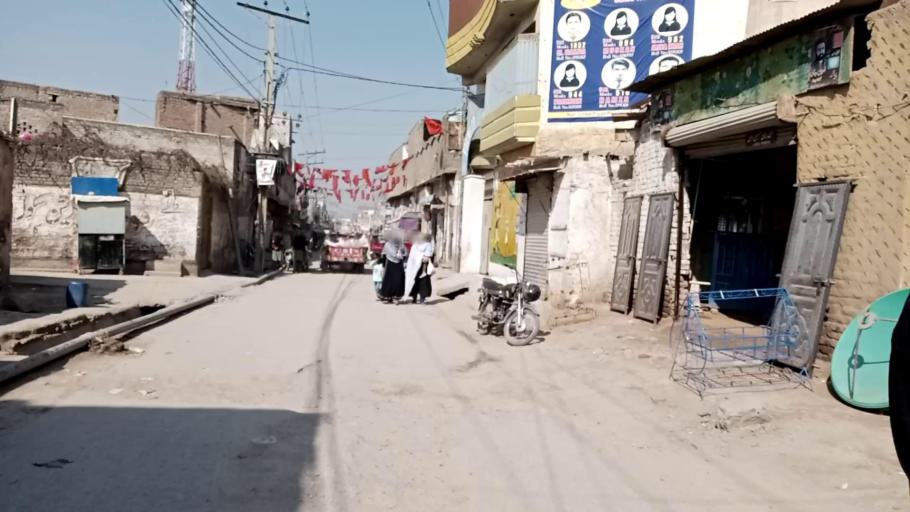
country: PK
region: Khyber Pakhtunkhwa
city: Peshawar
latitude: 34.0111
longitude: 71.5162
